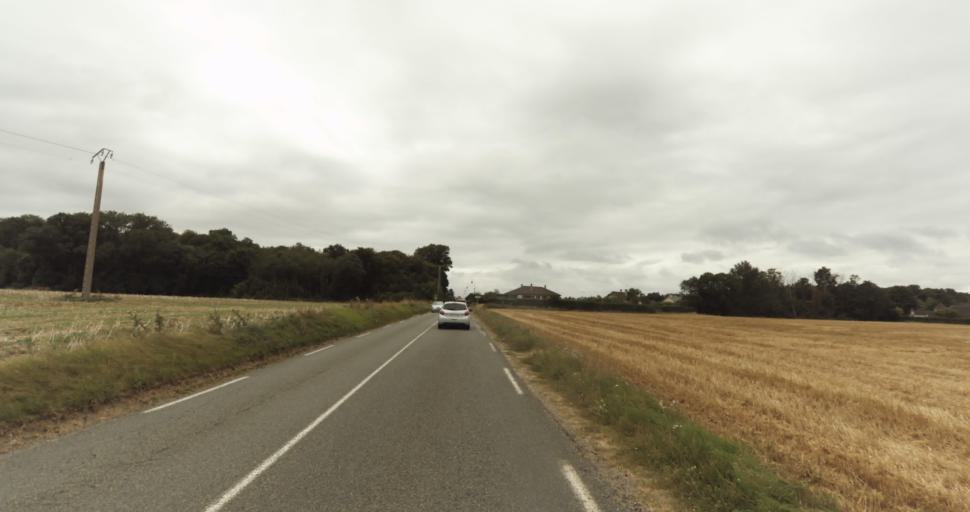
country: FR
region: Haute-Normandie
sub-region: Departement de l'Eure
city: Gravigny
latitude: 49.0335
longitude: 1.2003
